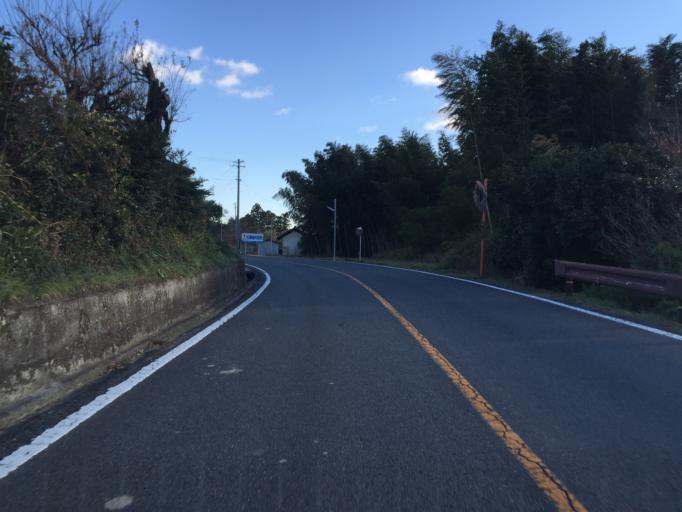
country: JP
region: Fukushima
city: Iwaki
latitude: 37.1468
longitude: 140.8338
